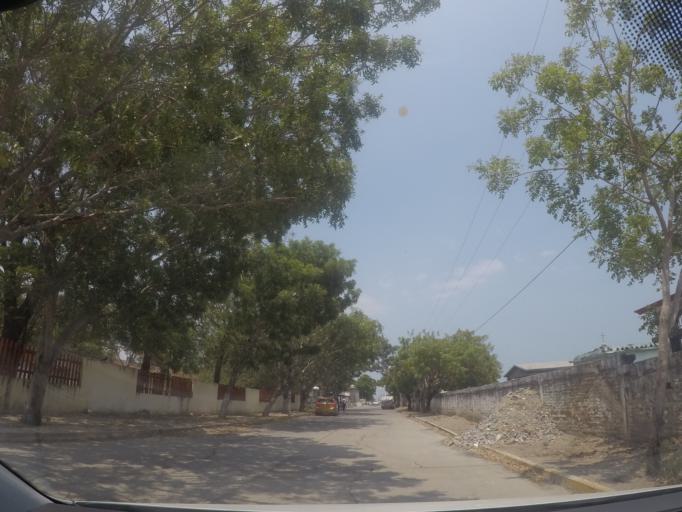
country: MX
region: Oaxaca
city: Asuncion Ixtaltepec
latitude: 16.5045
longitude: -95.0649
